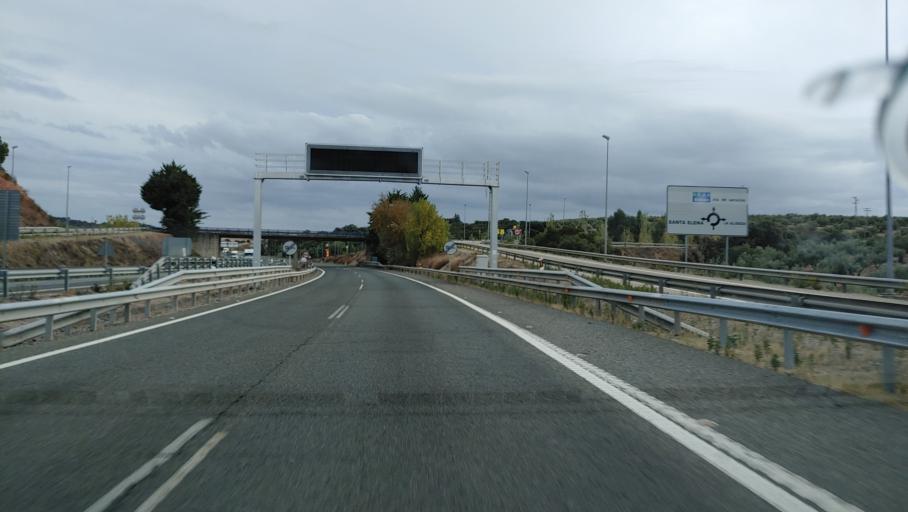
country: ES
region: Andalusia
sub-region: Provincia de Jaen
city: Santa Elena
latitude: 38.3397
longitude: -3.5455
